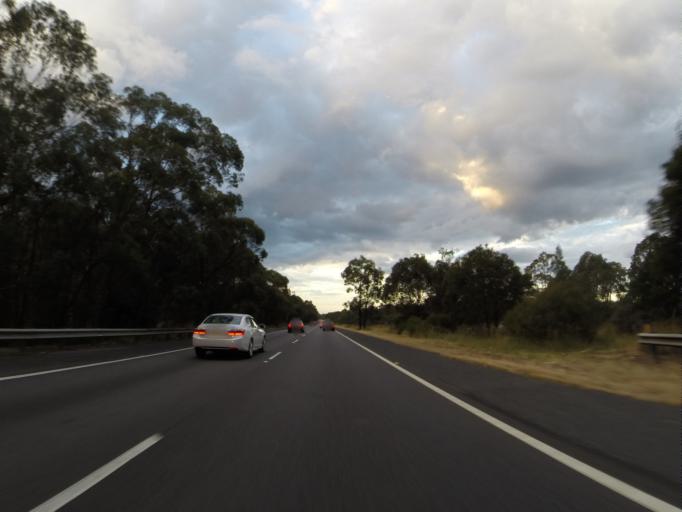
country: AU
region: New South Wales
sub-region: Wollondilly
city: Douglas Park
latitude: -34.2097
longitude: 150.6915
